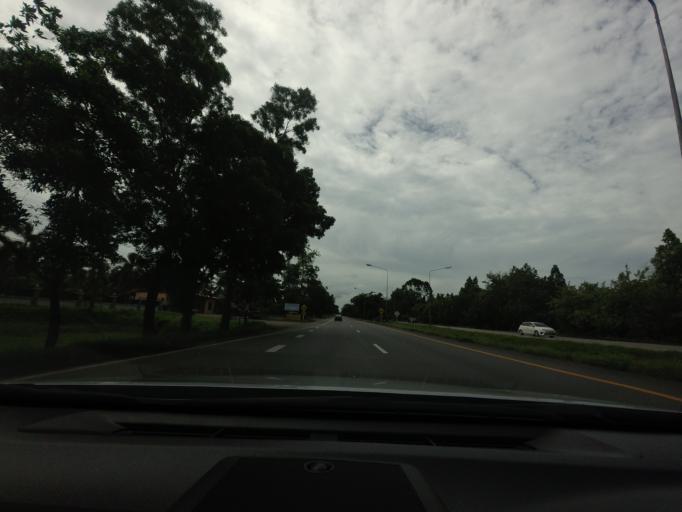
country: TH
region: Chumphon
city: Lamae
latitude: 9.7298
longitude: 99.1028
